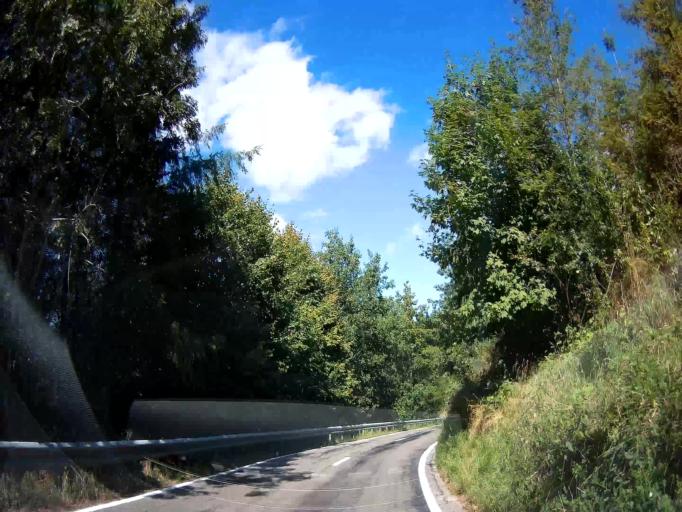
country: BE
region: Wallonia
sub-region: Province du Luxembourg
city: La Roche-en-Ardenne
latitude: 50.1665
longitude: 5.5913
